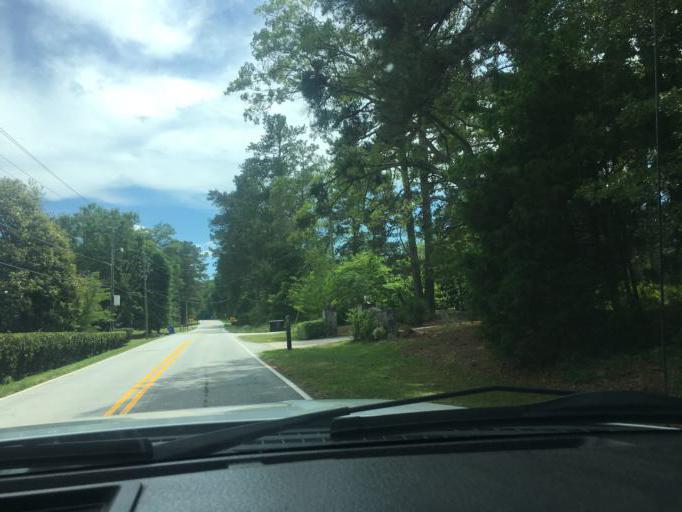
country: US
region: Georgia
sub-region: Rockdale County
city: Lakeview Estates
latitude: 33.7156
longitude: -84.0588
